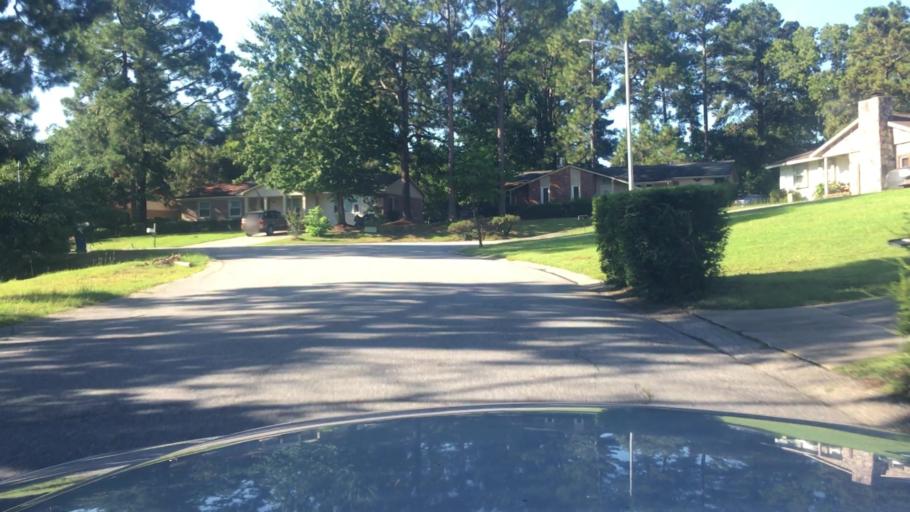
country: US
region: North Carolina
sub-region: Cumberland County
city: Fayetteville
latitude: 35.1373
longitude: -78.8909
